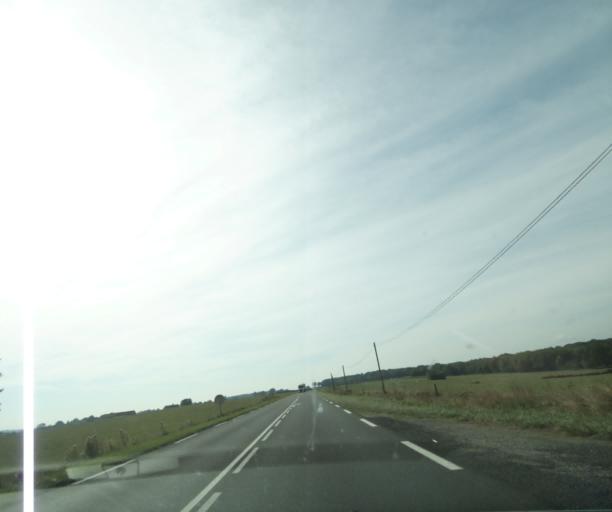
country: FR
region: Auvergne
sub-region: Departement de l'Allier
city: Molinet
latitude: 46.4489
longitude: 3.9153
